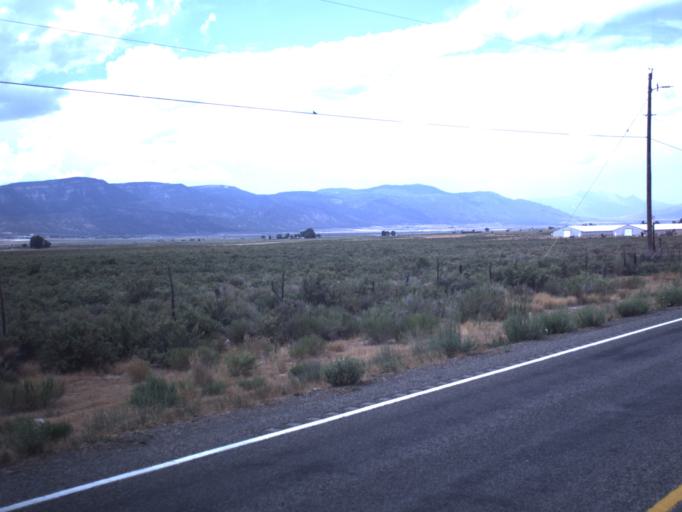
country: US
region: Utah
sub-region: Sanpete County
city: Ephraim
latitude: 39.4425
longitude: -111.5624
